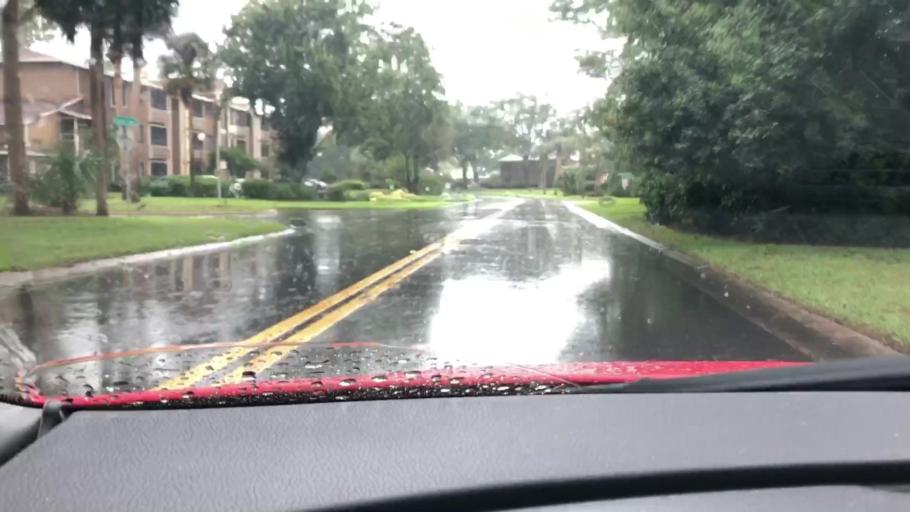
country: US
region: Florida
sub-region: Volusia County
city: South Daytona
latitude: 29.1666
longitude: -81.0471
